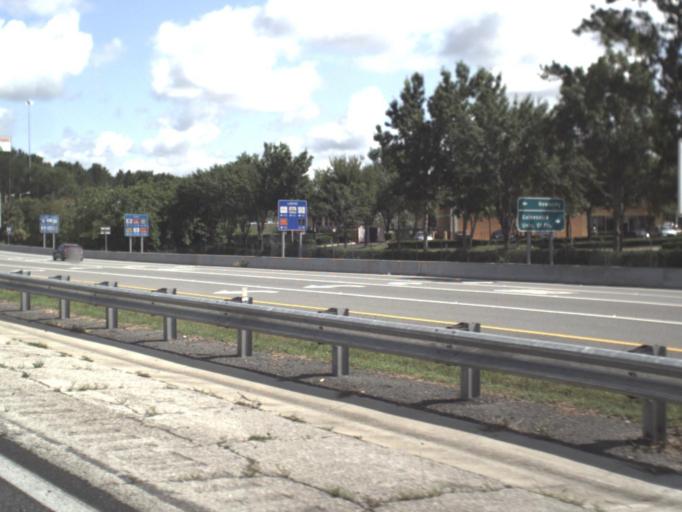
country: US
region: Florida
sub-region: Alachua County
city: Gainesville
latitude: 29.6574
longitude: -82.4169
